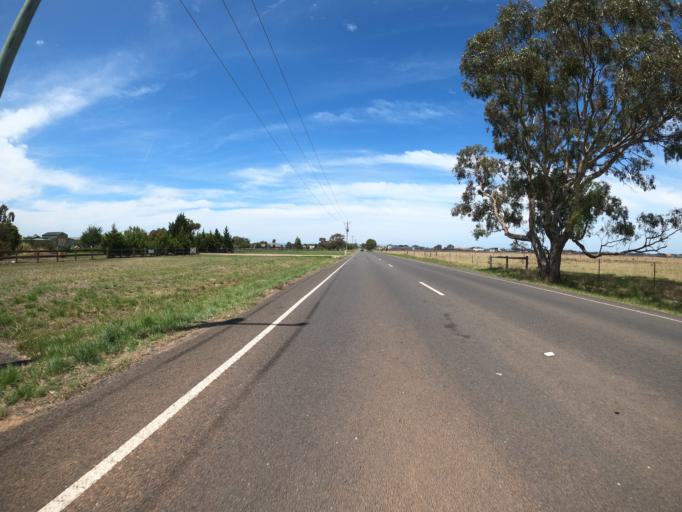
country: AU
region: Victoria
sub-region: Hume
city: Greenvale
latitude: -37.5632
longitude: 144.8863
